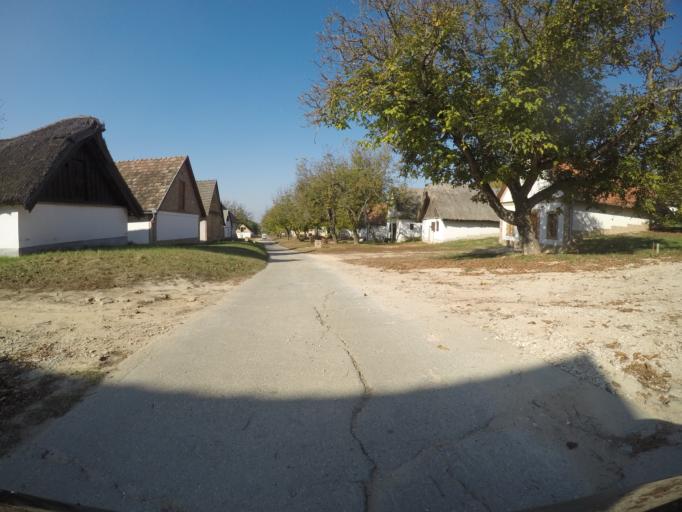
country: HU
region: Tolna
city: Nagydorog
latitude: 46.6346
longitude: 18.7053
